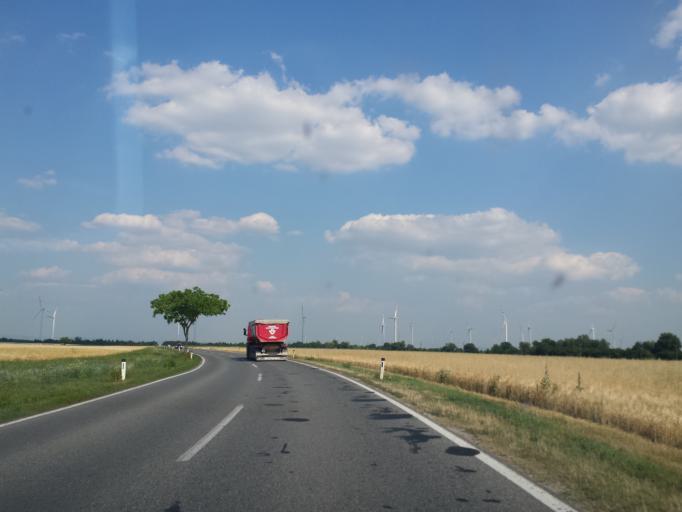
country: AT
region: Lower Austria
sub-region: Politischer Bezirk Ganserndorf
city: Markgrafneusiedl
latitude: 48.2633
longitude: 16.6378
